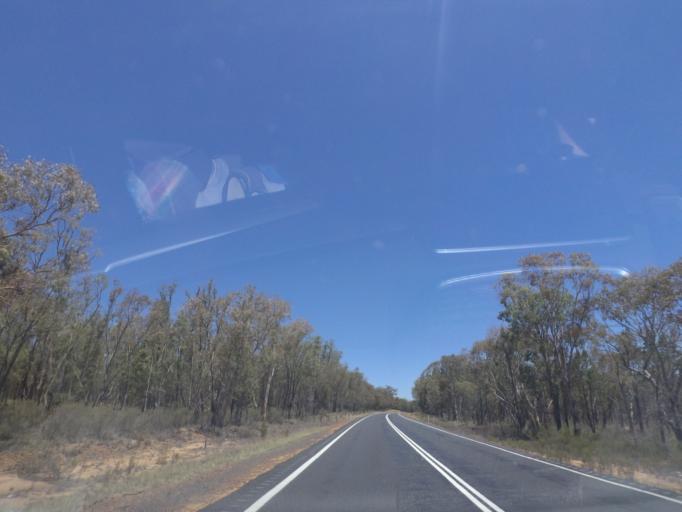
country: AU
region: New South Wales
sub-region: Warrumbungle Shire
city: Coonabarabran
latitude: -31.1910
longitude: 149.3537
